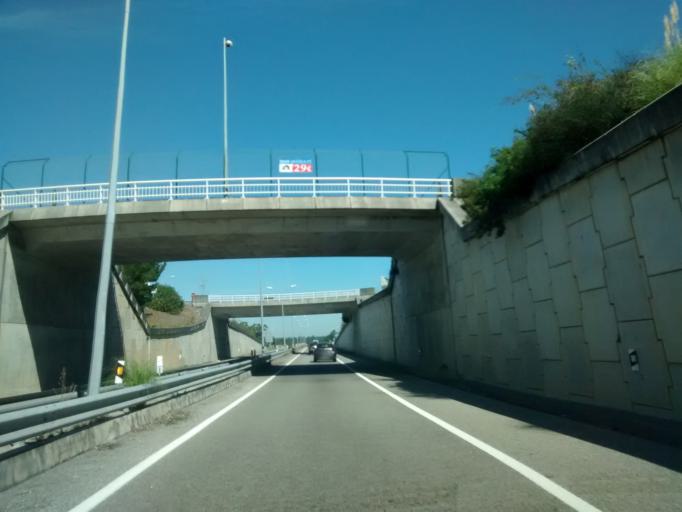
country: PT
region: Aveiro
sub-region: Oliveira do Bairro
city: Oliveira do Bairro
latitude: 40.5129
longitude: -8.4993
